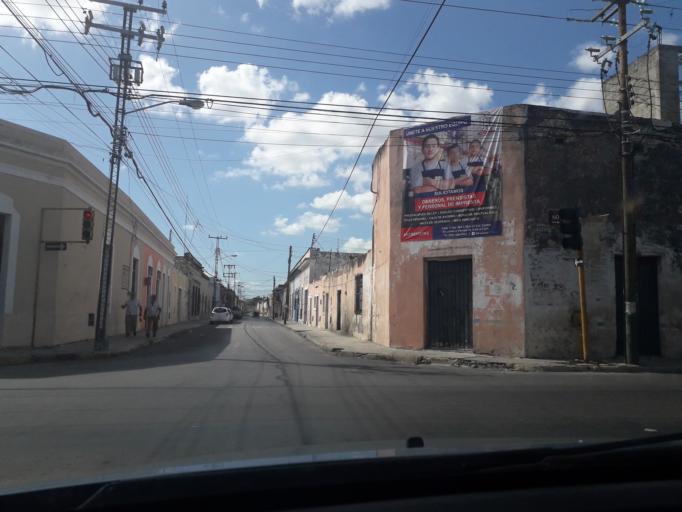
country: MX
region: Yucatan
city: Merida
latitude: 20.9598
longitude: -89.6245
